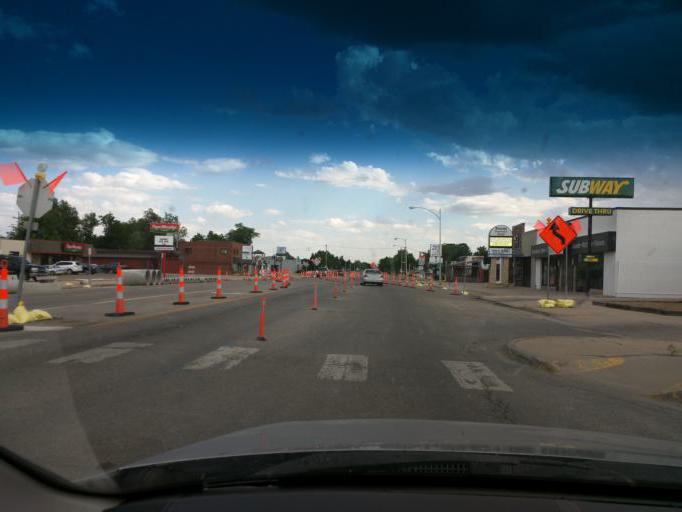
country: US
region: Kansas
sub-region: Reno County
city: Hutchinson
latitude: 38.0809
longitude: -97.9320
